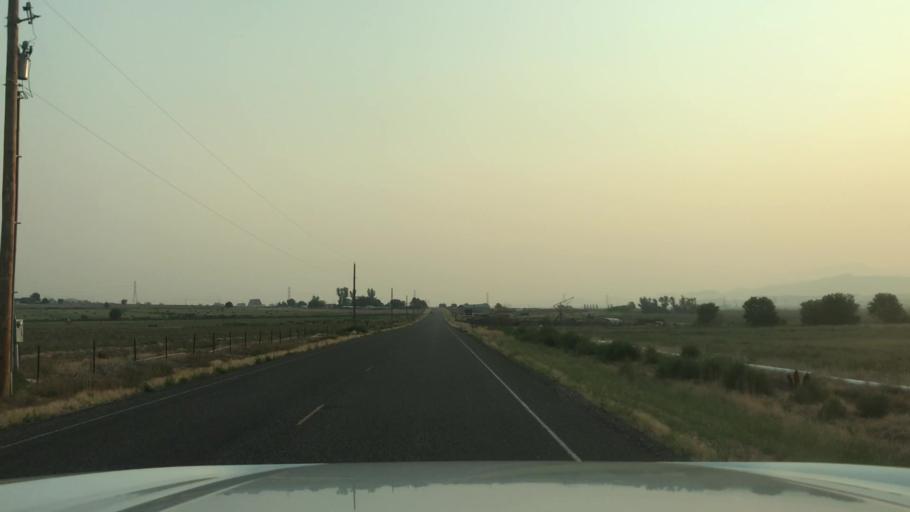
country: US
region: Utah
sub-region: Sevier County
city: Aurora
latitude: 38.8829
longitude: -111.9602
